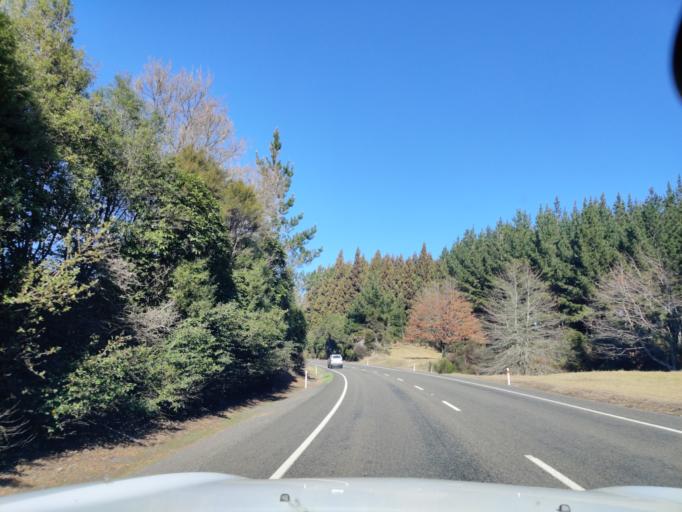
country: NZ
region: Waikato
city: Turangi
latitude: -39.0427
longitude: 175.8145
